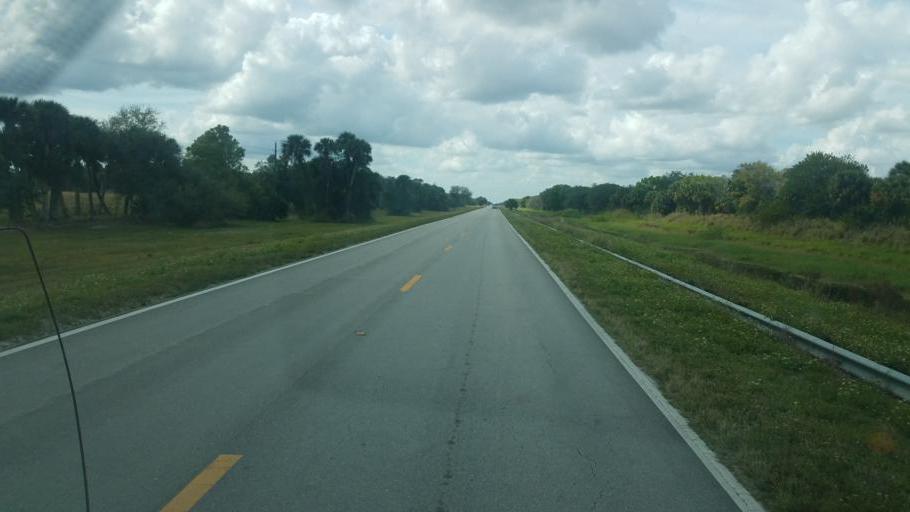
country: US
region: Florida
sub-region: Saint Lucie County
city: Lakewood Park
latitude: 27.4481
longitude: -80.5763
